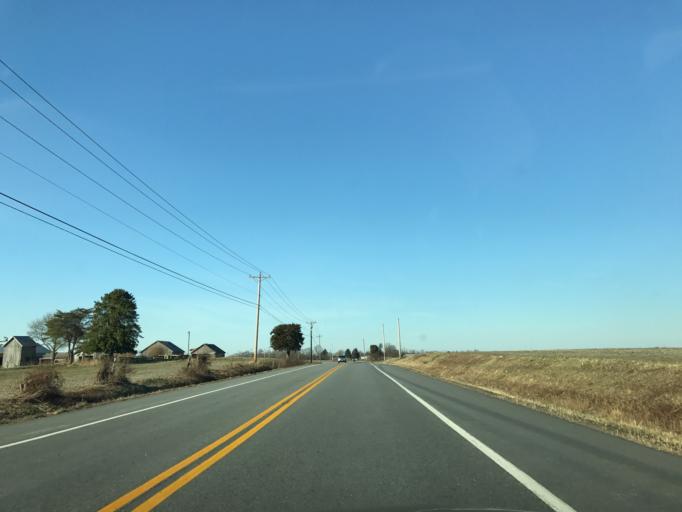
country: US
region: Maryland
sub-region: Queen Anne's County
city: Kingstown
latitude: 39.2096
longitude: -75.8636
